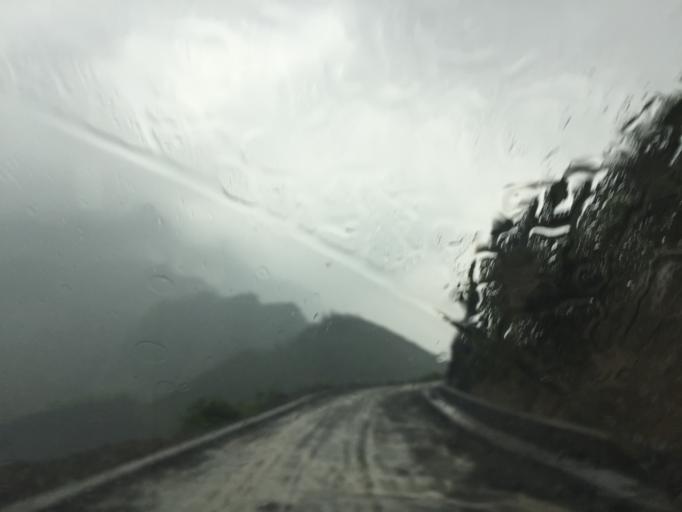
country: CN
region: Guizhou Sheng
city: Changfeng
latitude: 28.4391
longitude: 108.0796
